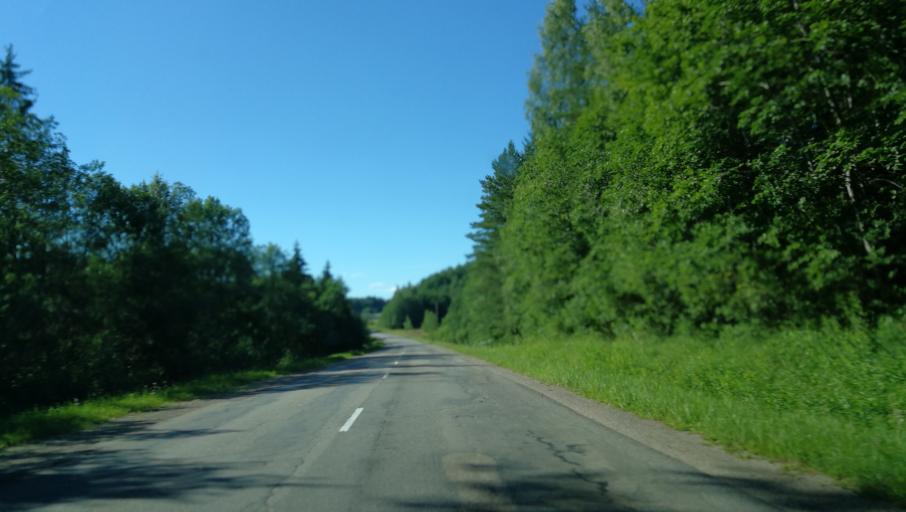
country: LV
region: Jaunpiebalga
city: Jaunpiebalga
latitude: 56.9757
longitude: 26.0424
